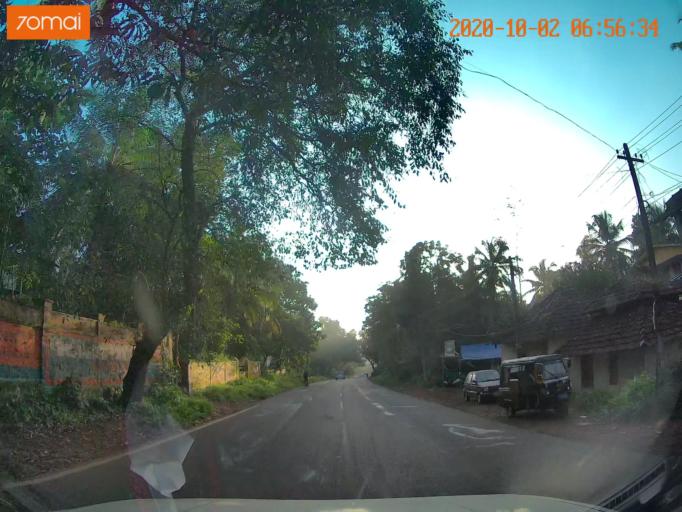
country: IN
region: Kerala
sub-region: Malappuram
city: Tirur
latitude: 10.8681
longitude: 76.0465
